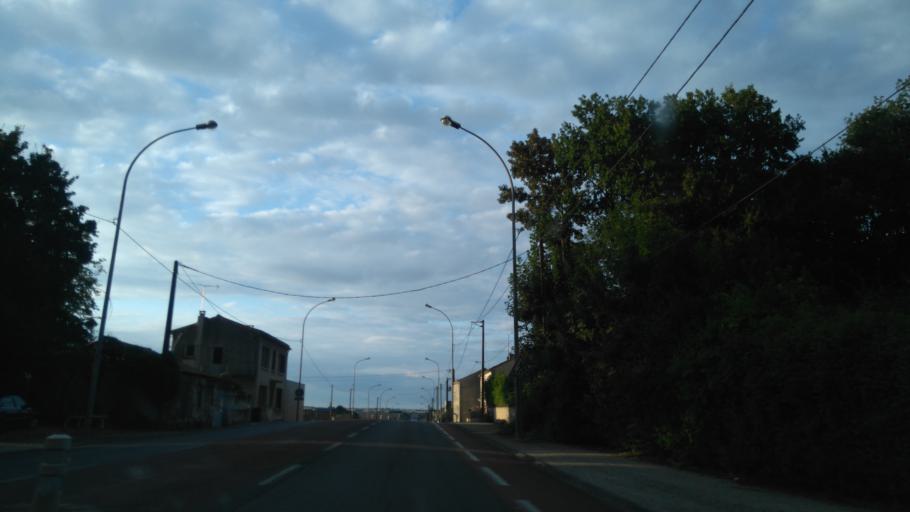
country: FR
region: Poitou-Charentes
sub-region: Departement de la Charente
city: Champniers
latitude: 45.7044
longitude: 0.1823
